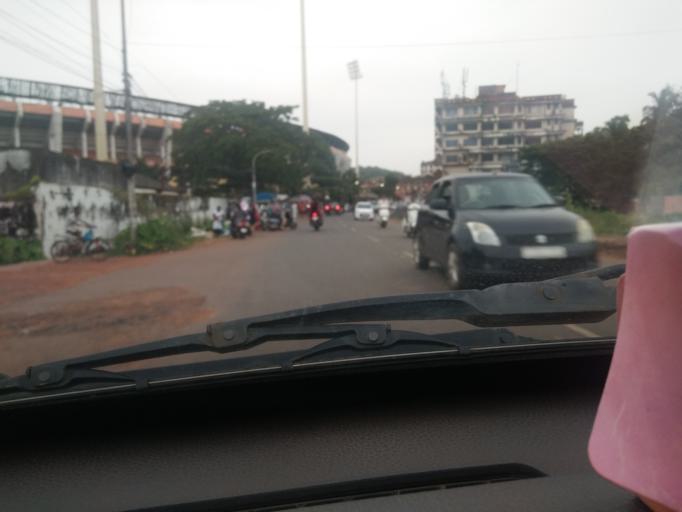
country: IN
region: Goa
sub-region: South Goa
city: Madgaon
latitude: 15.2880
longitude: 73.9634
